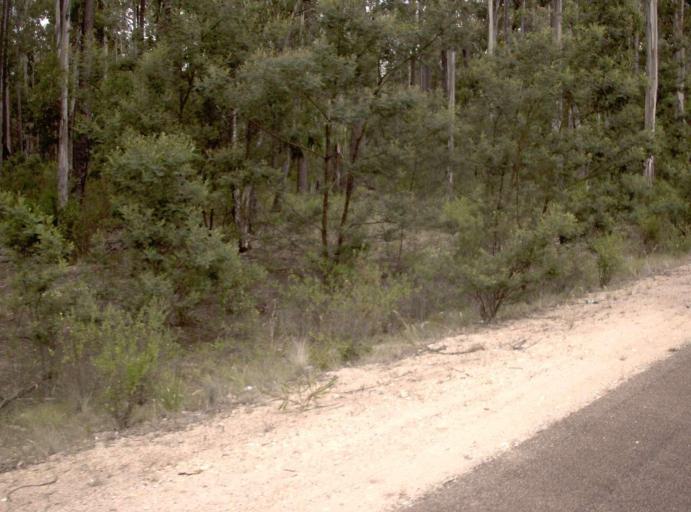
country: AU
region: Victoria
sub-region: East Gippsland
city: Lakes Entrance
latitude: -37.7166
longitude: 148.0765
